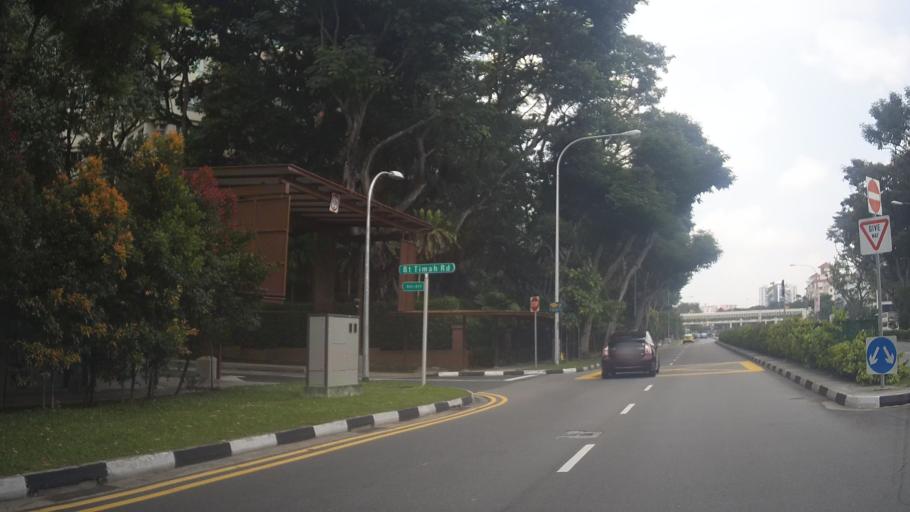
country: SG
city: Singapore
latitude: 1.3347
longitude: 103.7866
